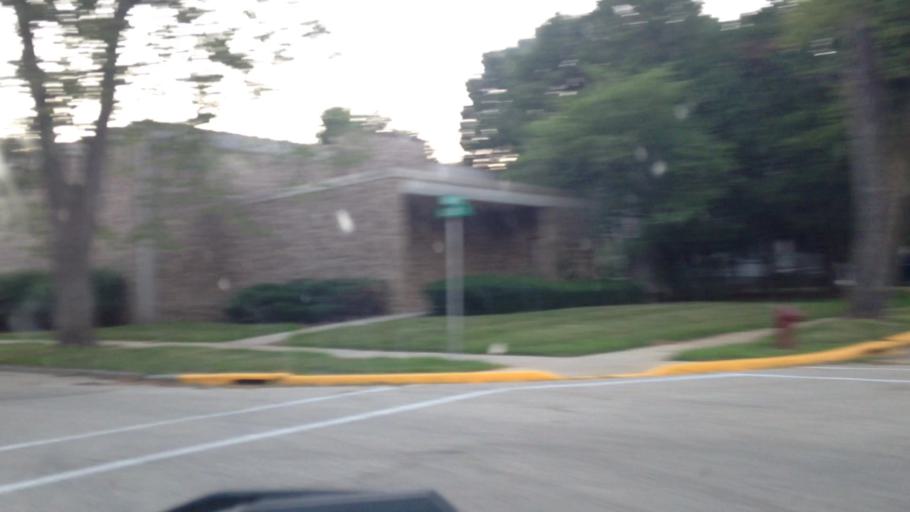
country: US
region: Wisconsin
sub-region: Dodge County
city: Mayville
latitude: 43.4948
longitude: -88.5470
